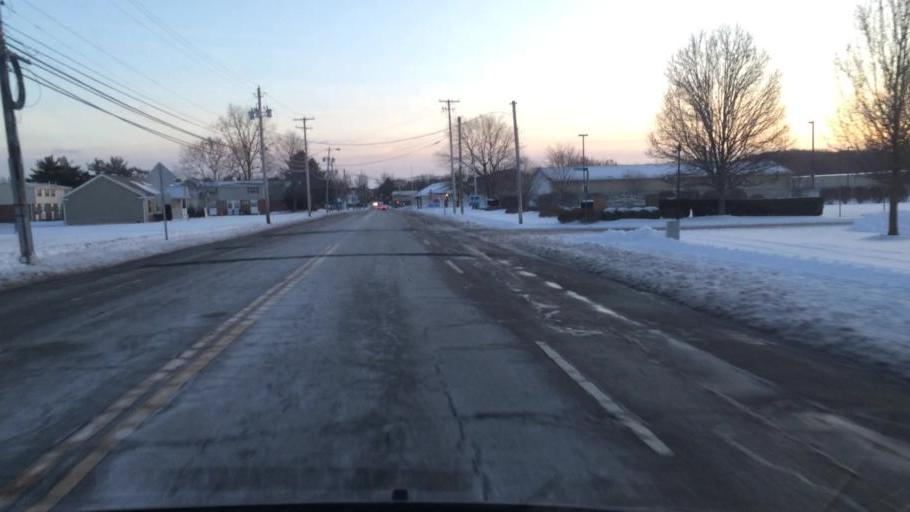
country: US
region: Ohio
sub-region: Summit County
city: Barberton
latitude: 41.0066
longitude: -81.6009
